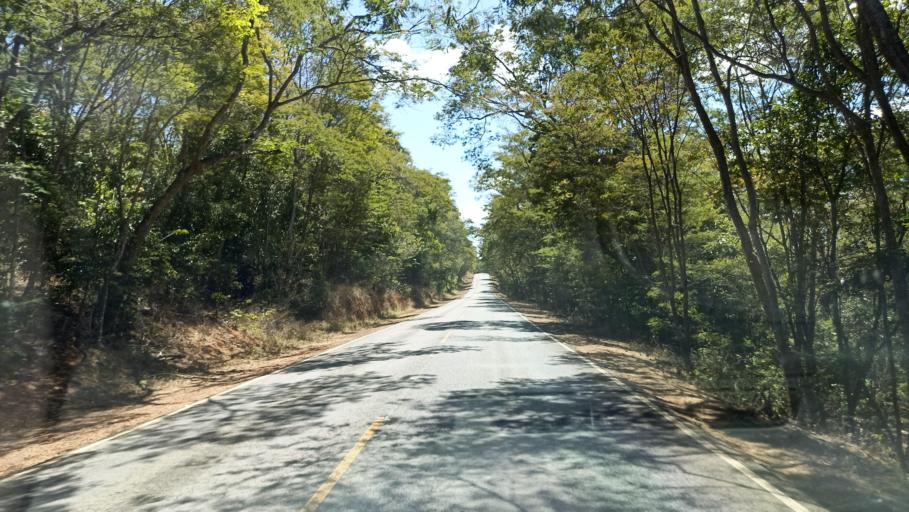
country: BR
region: Bahia
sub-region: Andarai
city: Vera Cruz
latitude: -12.7791
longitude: -41.3296
